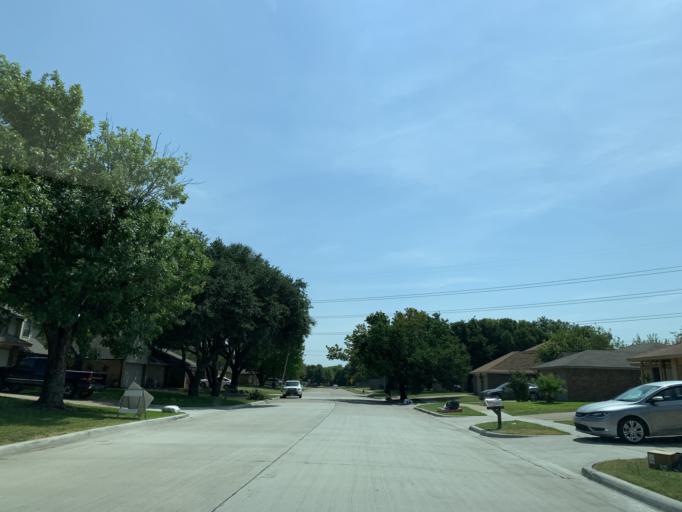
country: US
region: Texas
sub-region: Dallas County
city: Grand Prairie
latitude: 32.6661
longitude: -97.0386
